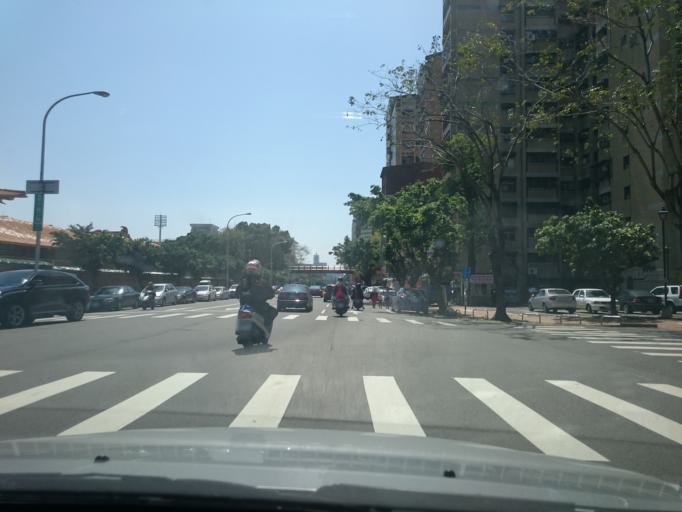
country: TW
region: Taiwan
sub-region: Taichung City
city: Taichung
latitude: 24.1550
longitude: 120.6897
